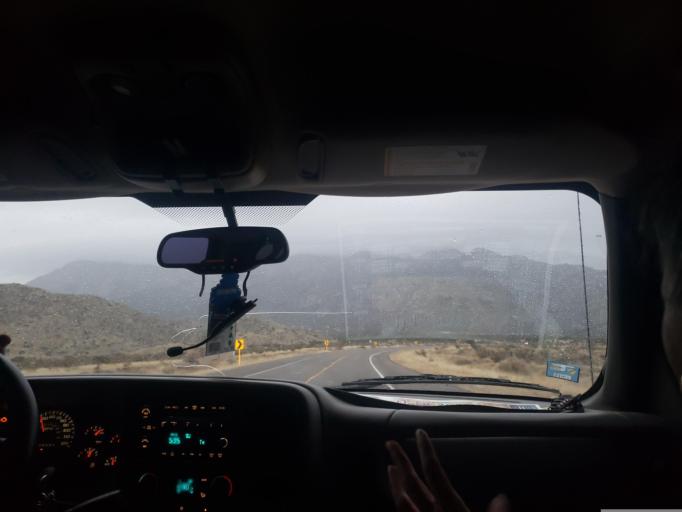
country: US
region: New Mexico
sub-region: Bernalillo County
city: Sandia Heights
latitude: 35.2013
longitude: -106.5119
